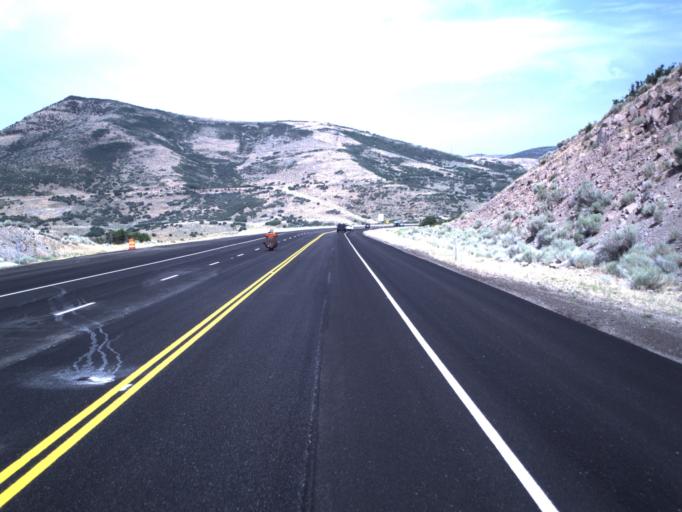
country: US
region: Utah
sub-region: Summit County
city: Park City
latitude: 40.6510
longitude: -111.4055
